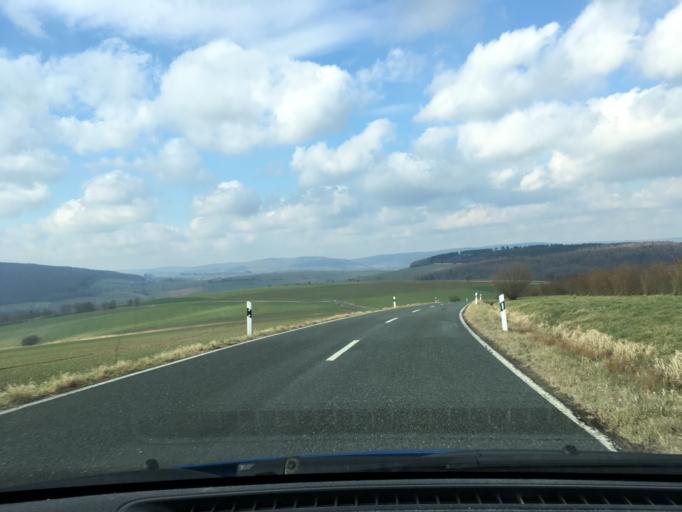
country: DE
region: Lower Saxony
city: Uslar
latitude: 51.6110
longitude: 9.6311
